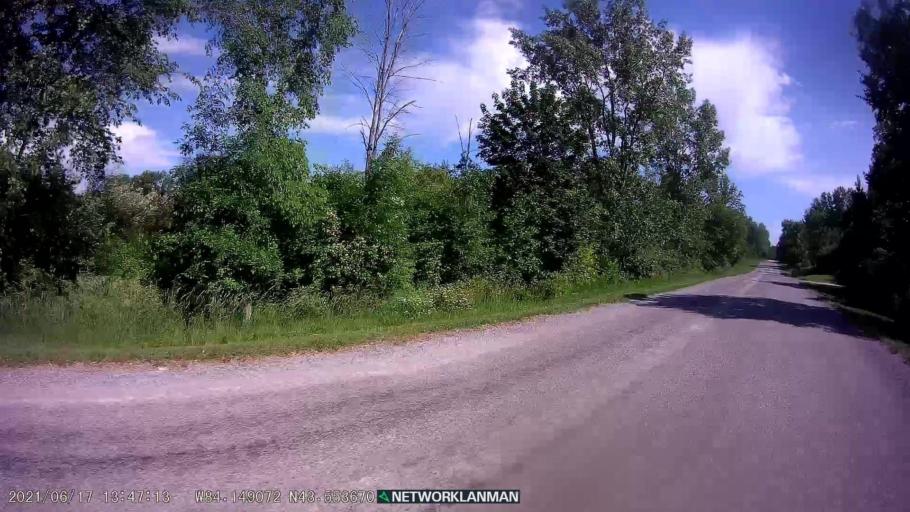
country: US
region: Michigan
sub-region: Saginaw County
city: Freeland
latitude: 43.5532
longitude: -84.1491
